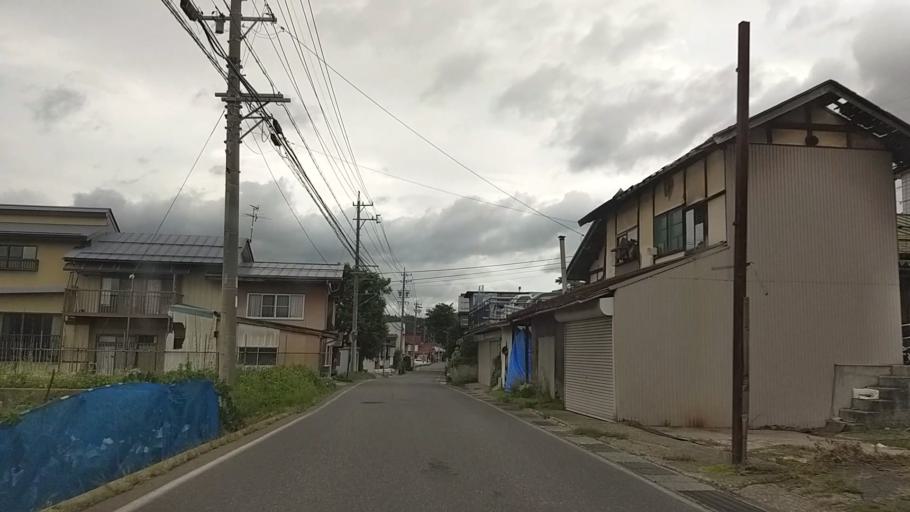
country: JP
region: Nagano
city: Iiyama
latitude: 36.8036
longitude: 138.3591
